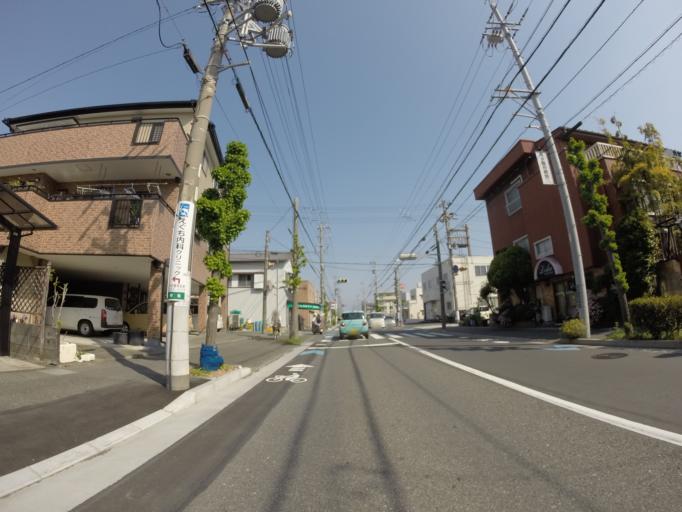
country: JP
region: Shizuoka
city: Shizuoka-shi
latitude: 34.9962
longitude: 138.4899
